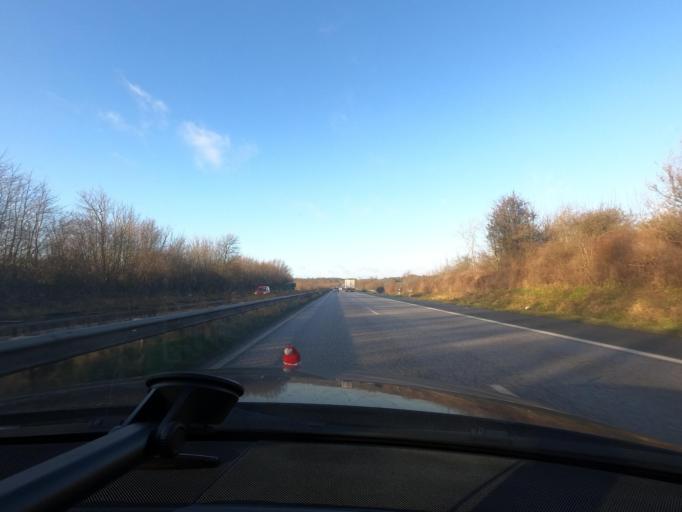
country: DE
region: Schleswig-Holstein
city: Dannewerk
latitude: 54.4986
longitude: 9.5137
